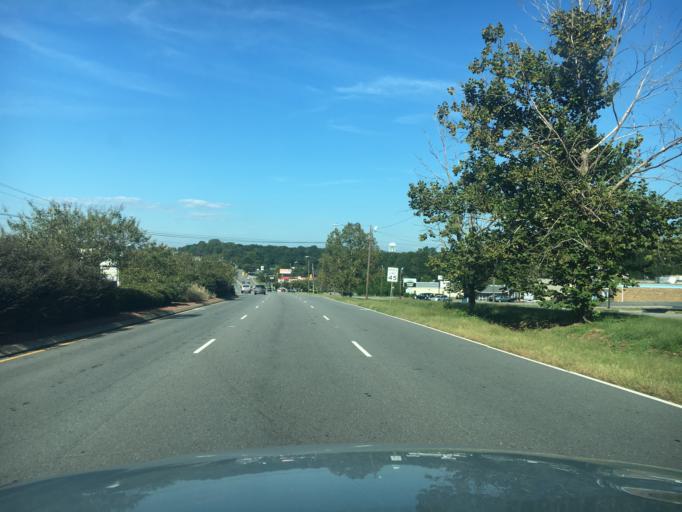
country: US
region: North Carolina
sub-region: Catawba County
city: Hickory
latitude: 35.7206
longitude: -81.3481
